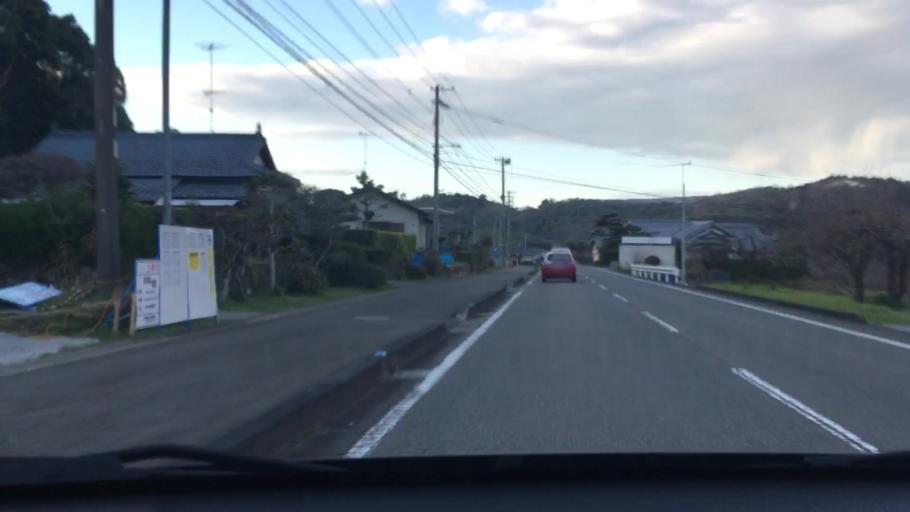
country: JP
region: Oita
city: Bungo-Takada-shi
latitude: 33.4988
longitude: 131.3760
